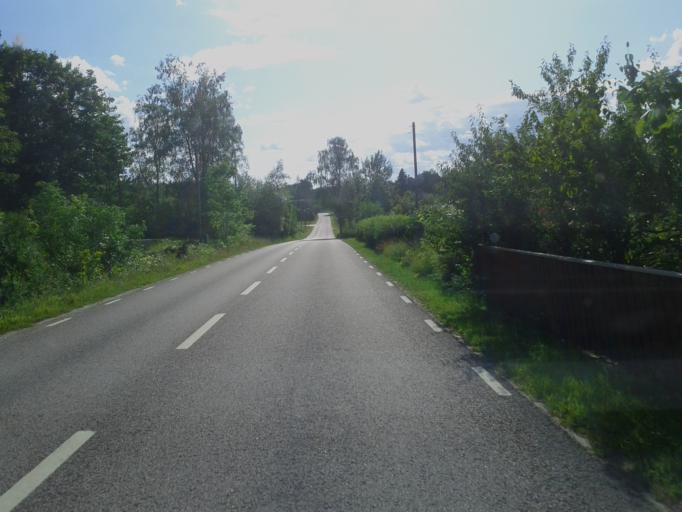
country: SE
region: Vaestmanland
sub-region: Sala Kommun
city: Sala
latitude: 59.9118
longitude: 16.5630
